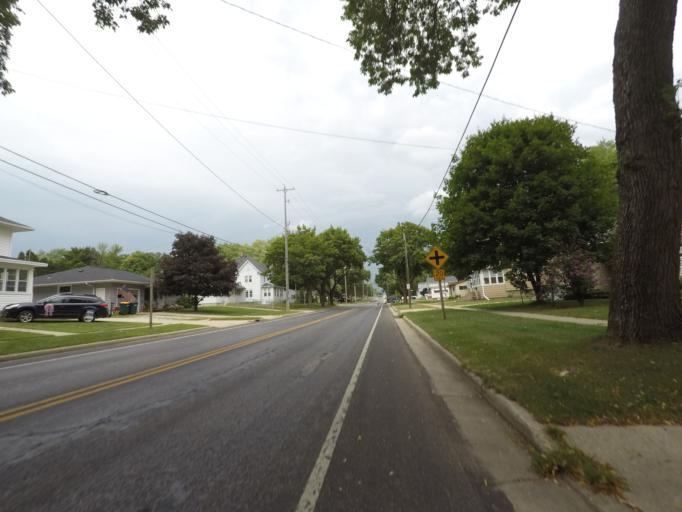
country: US
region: Wisconsin
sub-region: Jefferson County
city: Fort Atkinson
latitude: 42.9388
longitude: -88.8386
